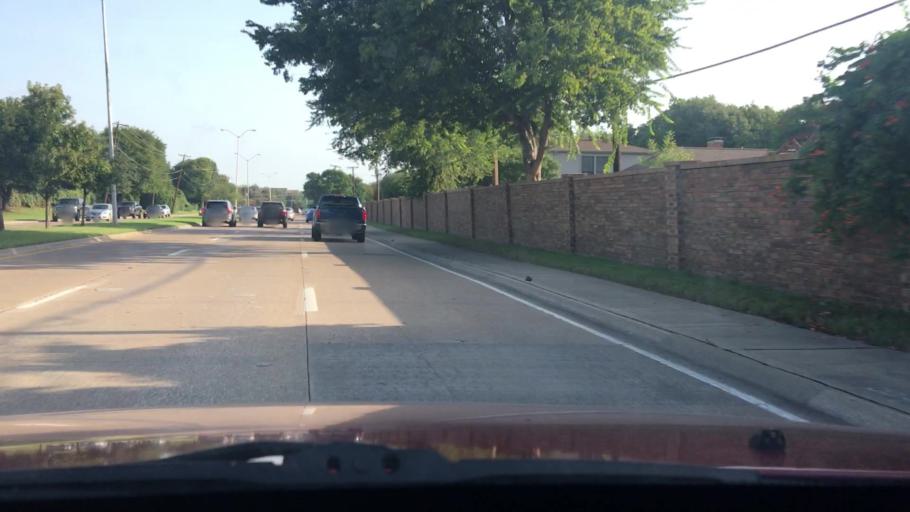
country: US
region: Texas
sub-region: Dallas County
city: Addison
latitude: 32.9795
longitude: -96.8043
